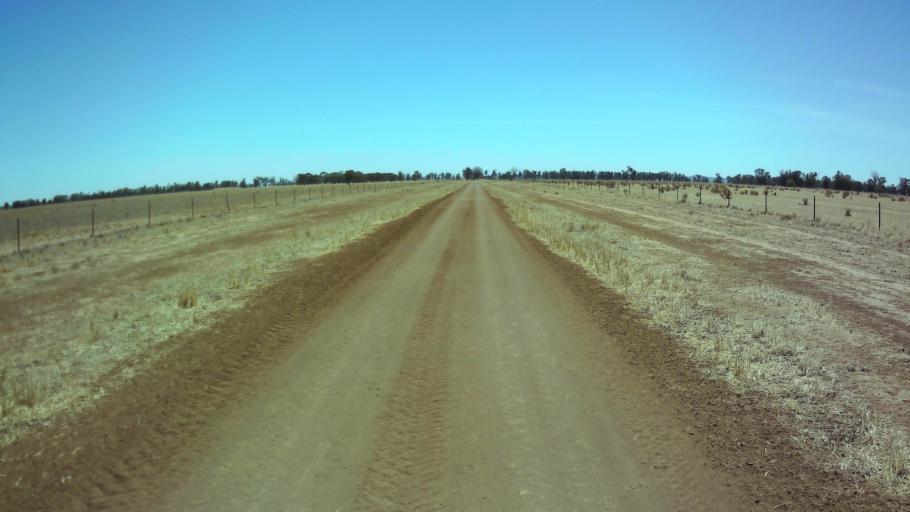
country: AU
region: New South Wales
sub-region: Weddin
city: Grenfell
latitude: -33.9838
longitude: 147.7355
